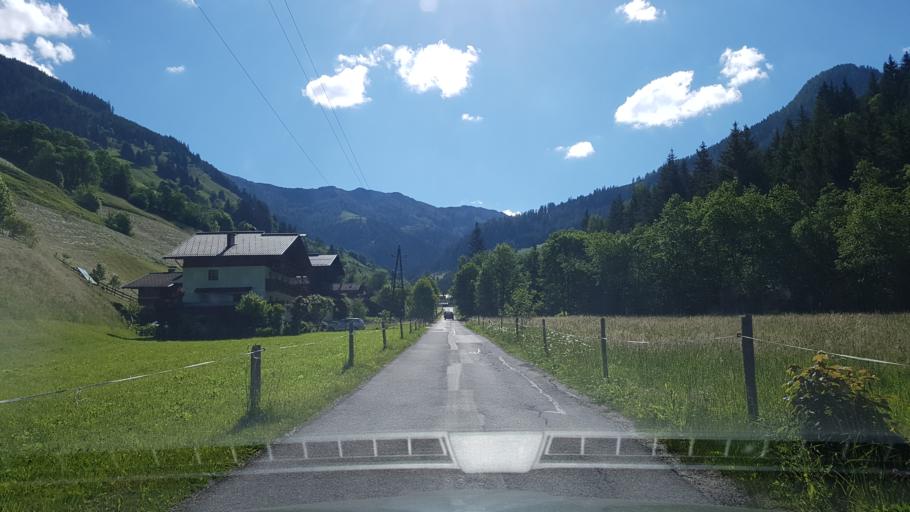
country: AT
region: Salzburg
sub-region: Politischer Bezirk Sankt Johann im Pongau
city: Huttschlag
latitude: 47.2353
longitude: 13.2381
